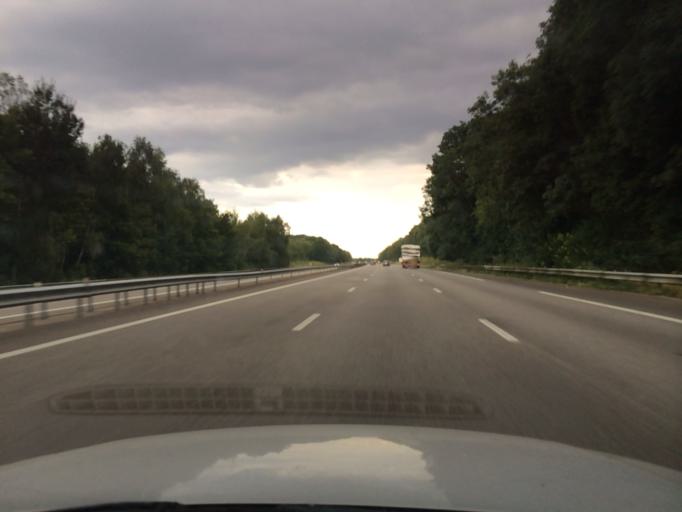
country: FR
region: Haute-Normandie
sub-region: Departement de l'Eure
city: Saint-Aubin-sur-Gaillon
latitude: 49.1542
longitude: 1.2783
